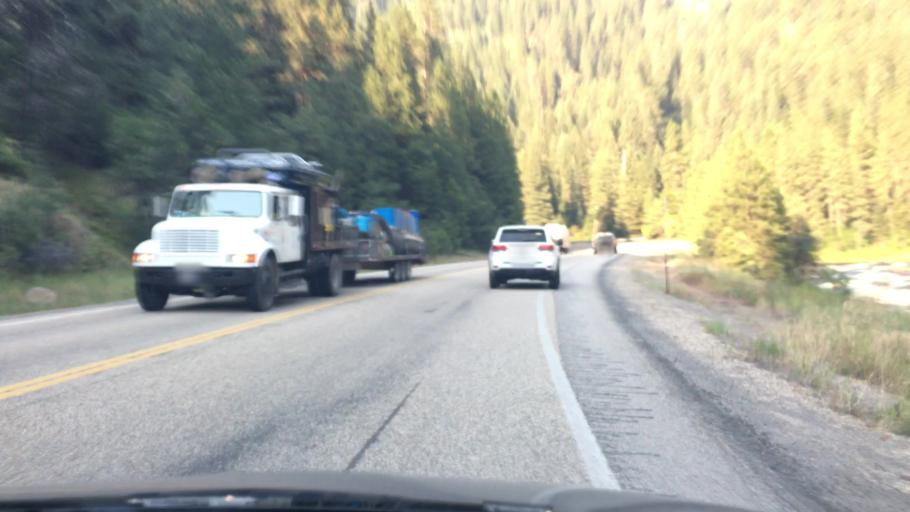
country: US
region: Idaho
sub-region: Valley County
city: Cascade
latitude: 44.1772
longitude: -116.1173
